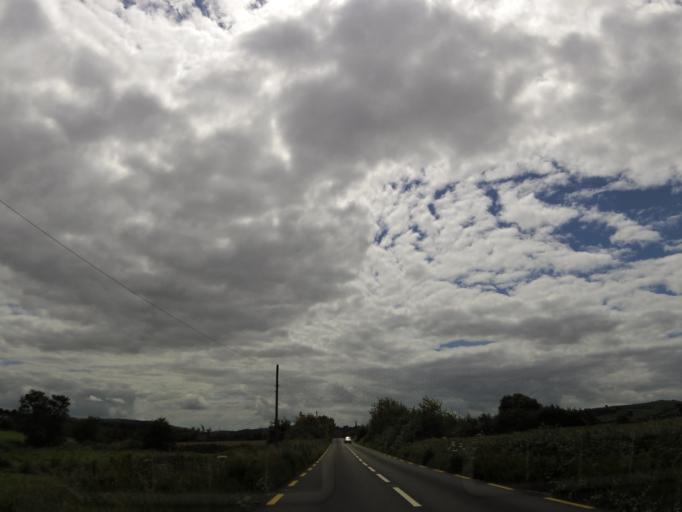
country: IE
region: Munster
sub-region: North Tipperary
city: Nenagh
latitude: 52.7870
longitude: -8.0354
